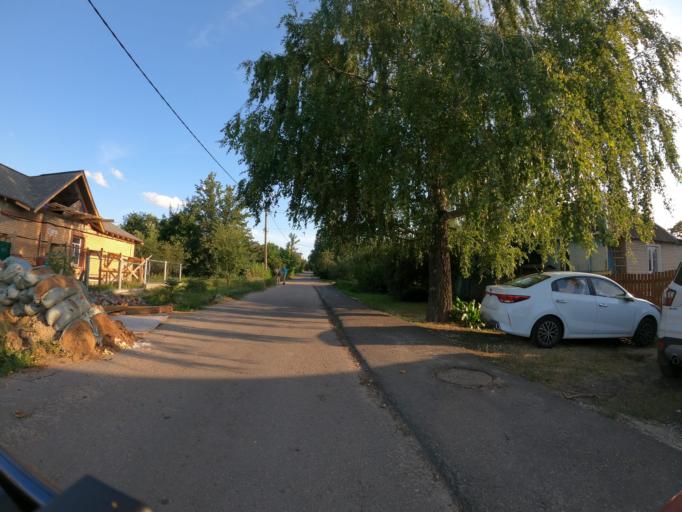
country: RU
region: Moskovskaya
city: Raduzhnyy
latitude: 55.1106
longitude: 38.7323
